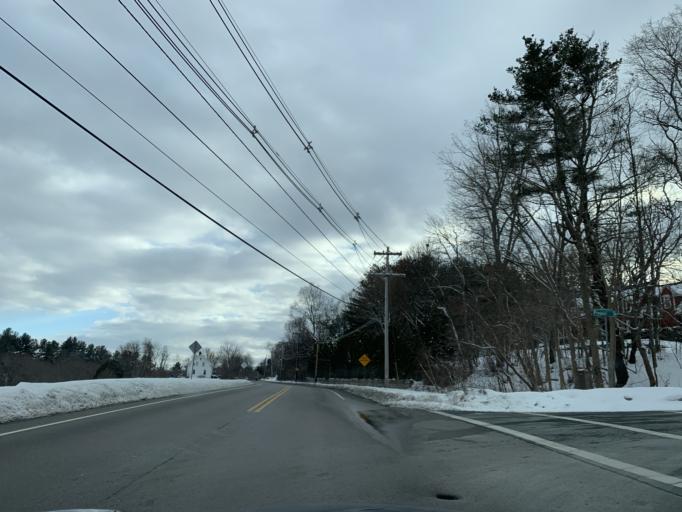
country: US
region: Massachusetts
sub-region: Norfolk County
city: Franklin
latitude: 42.0537
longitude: -71.4349
